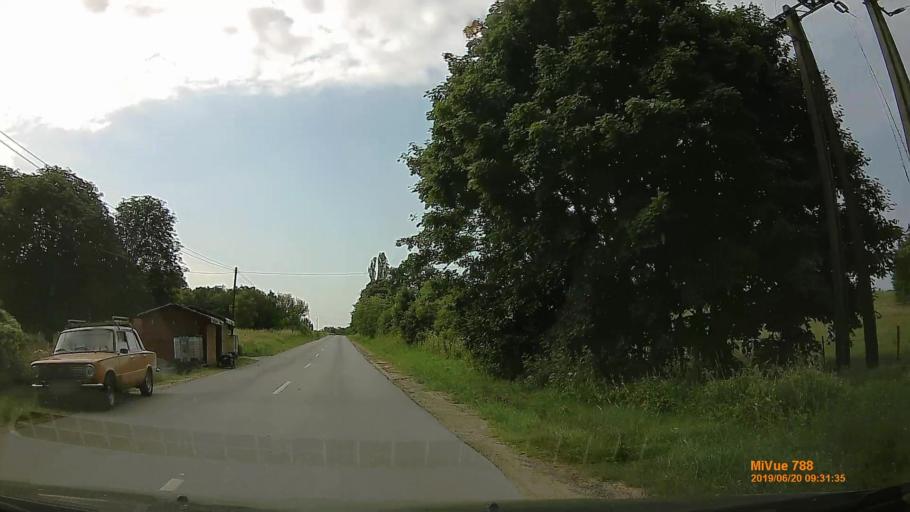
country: HU
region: Baranya
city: Pecsvarad
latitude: 46.1437
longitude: 18.4052
